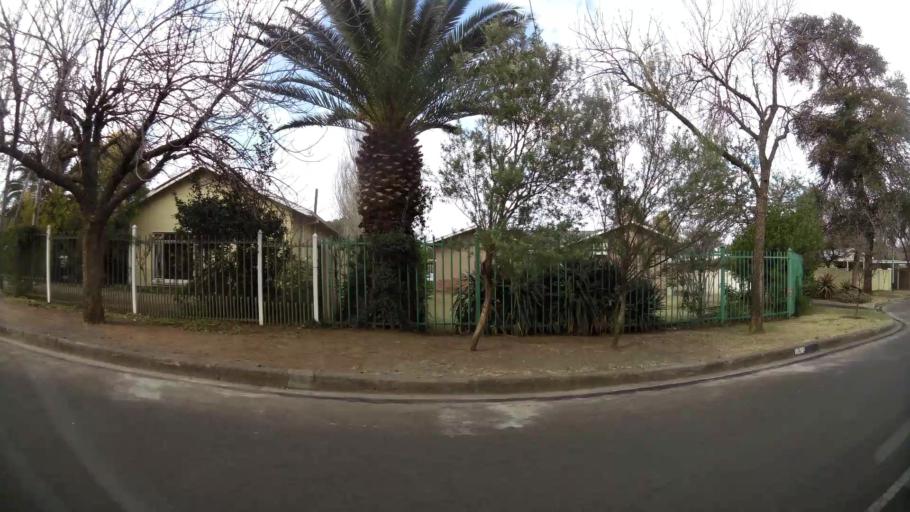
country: ZA
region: Orange Free State
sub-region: Mangaung Metropolitan Municipality
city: Bloemfontein
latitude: -29.0836
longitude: 26.2082
